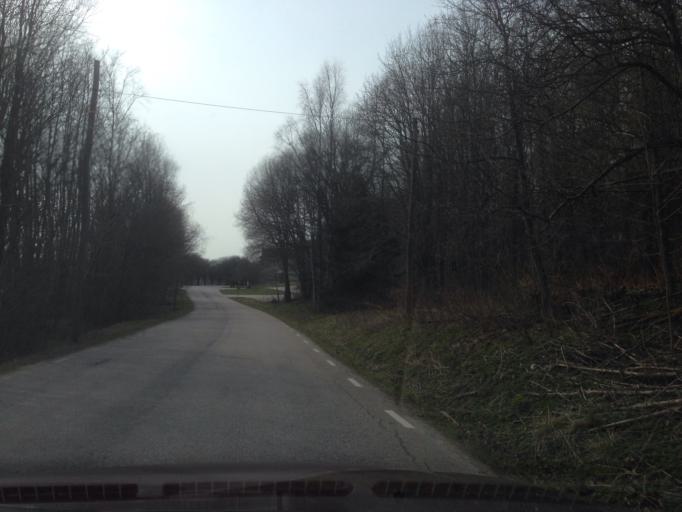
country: SE
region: Dalarna
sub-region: Ludvika Kommun
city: Grangesberg
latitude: 60.0825
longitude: 14.9909
